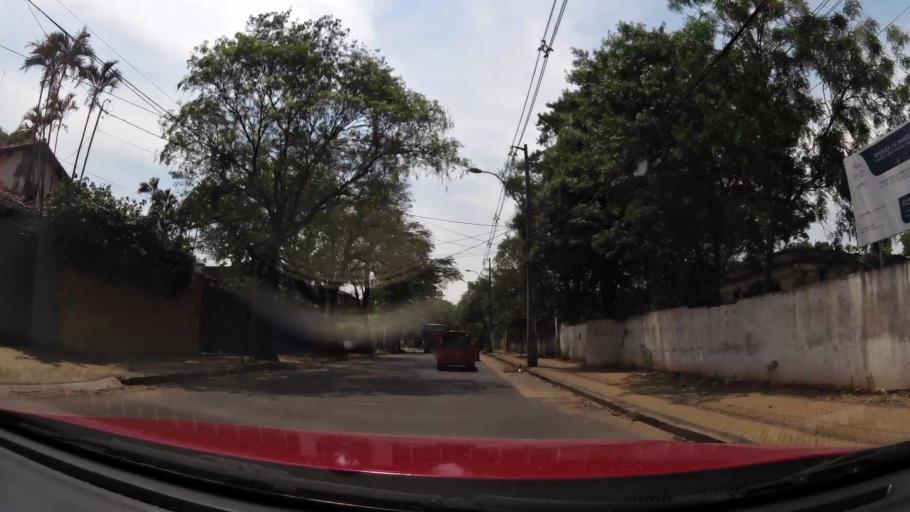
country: PY
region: Asuncion
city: Asuncion
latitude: -25.2811
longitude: -57.5943
